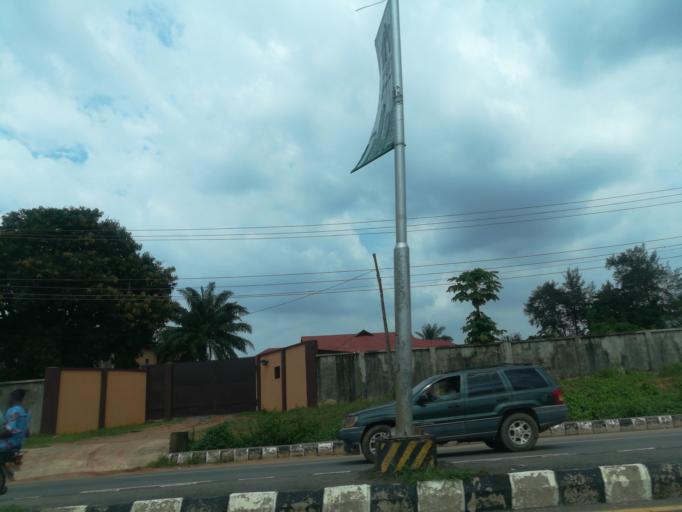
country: NG
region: Oyo
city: Ibadan
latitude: 7.3979
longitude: 3.8760
